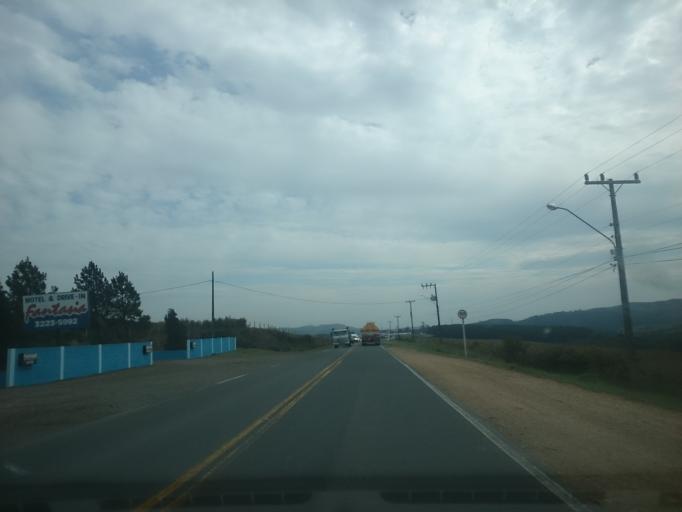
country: BR
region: Santa Catarina
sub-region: Lages
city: Lages
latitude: -27.7676
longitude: -50.3272
